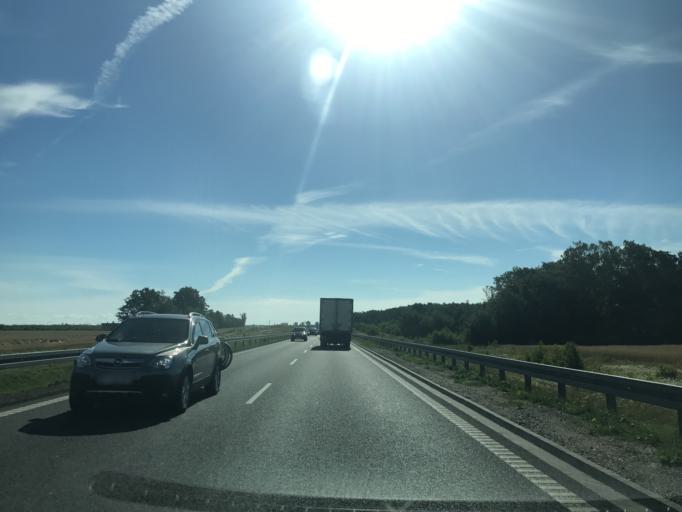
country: PL
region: Pomeranian Voivodeship
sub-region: Powiat chojnicki
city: Chojnice
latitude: 53.6841
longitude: 17.5094
